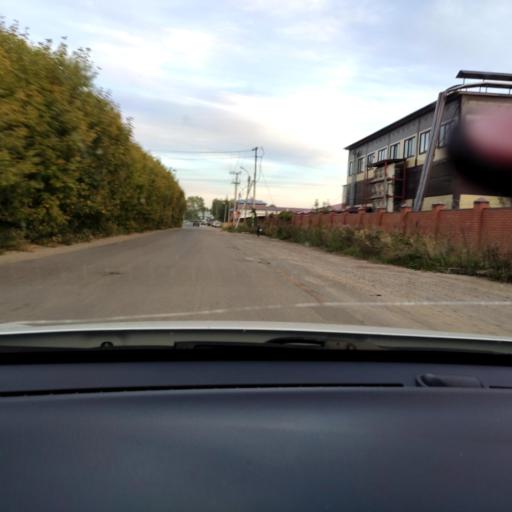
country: RU
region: Tatarstan
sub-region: Zelenodol'skiy Rayon
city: Zelenodolsk
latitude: 55.8382
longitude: 48.5269
